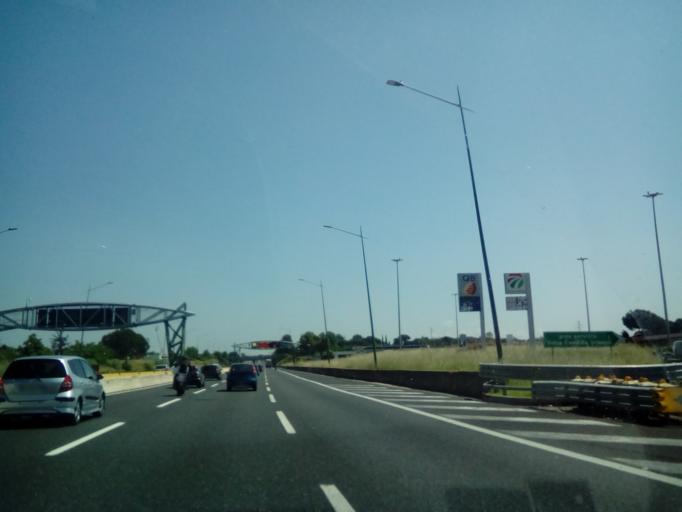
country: IT
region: Latium
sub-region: Citta metropolitana di Roma Capitale
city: Valle Santa
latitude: 41.9580
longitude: 12.3867
